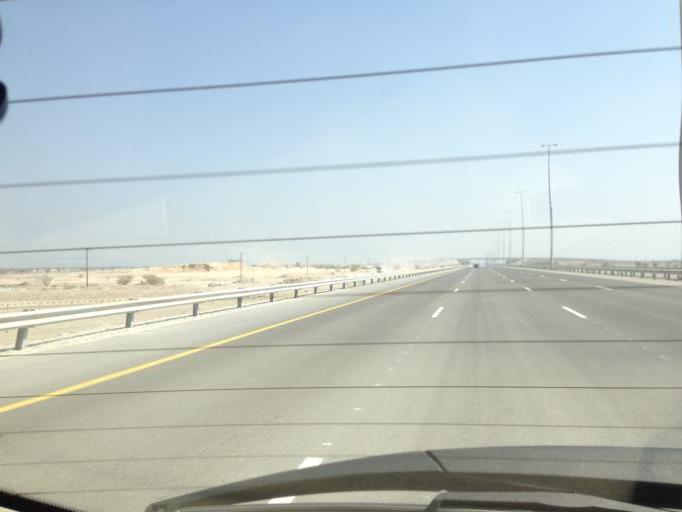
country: OM
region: Al Batinah
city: Barka'
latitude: 23.6171
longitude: 57.8365
